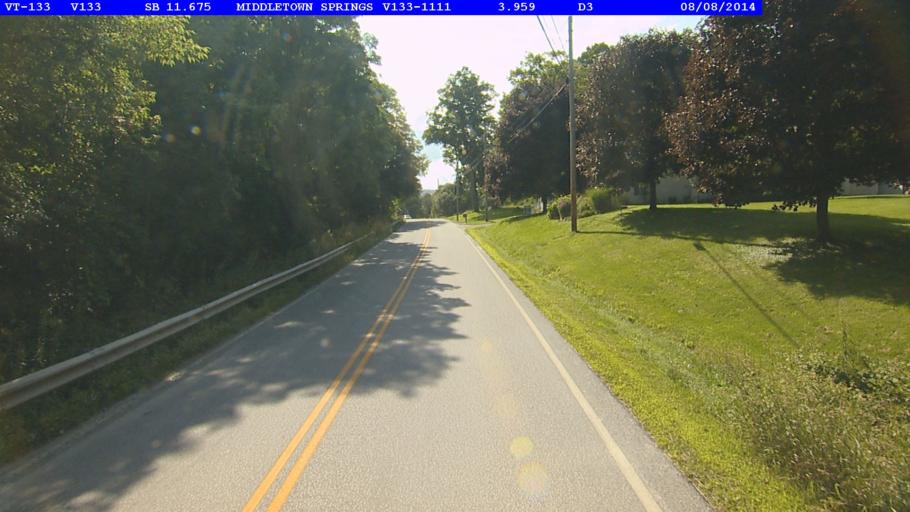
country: US
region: Vermont
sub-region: Rutland County
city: West Rutland
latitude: 43.4858
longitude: -73.1121
